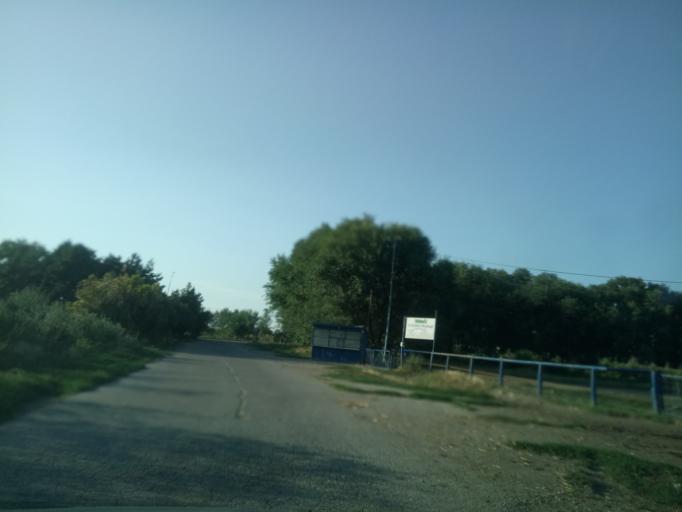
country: RS
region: Autonomna Pokrajina Vojvodina
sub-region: Sremski Okrug
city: Stara Pazova
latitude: 44.9958
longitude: 20.1619
